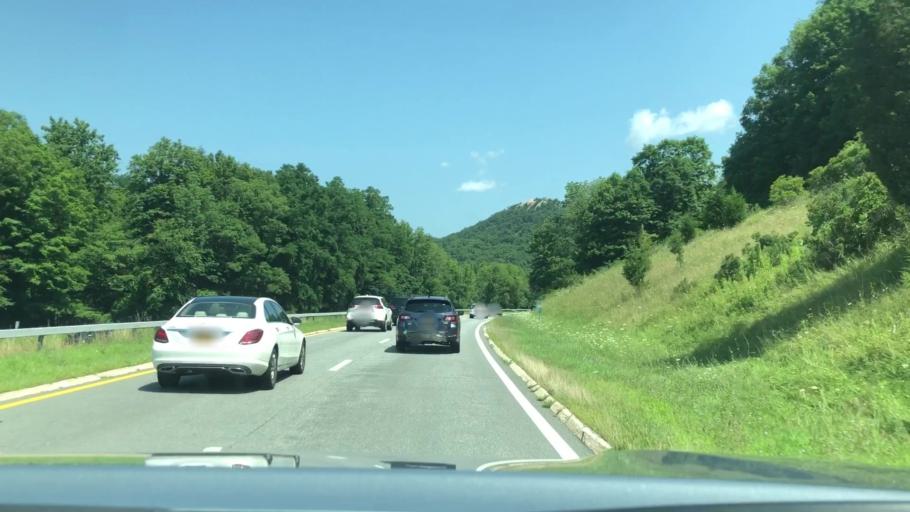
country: US
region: New York
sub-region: Orange County
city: Fort Montgomery
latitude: 41.3177
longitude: -74.0155
